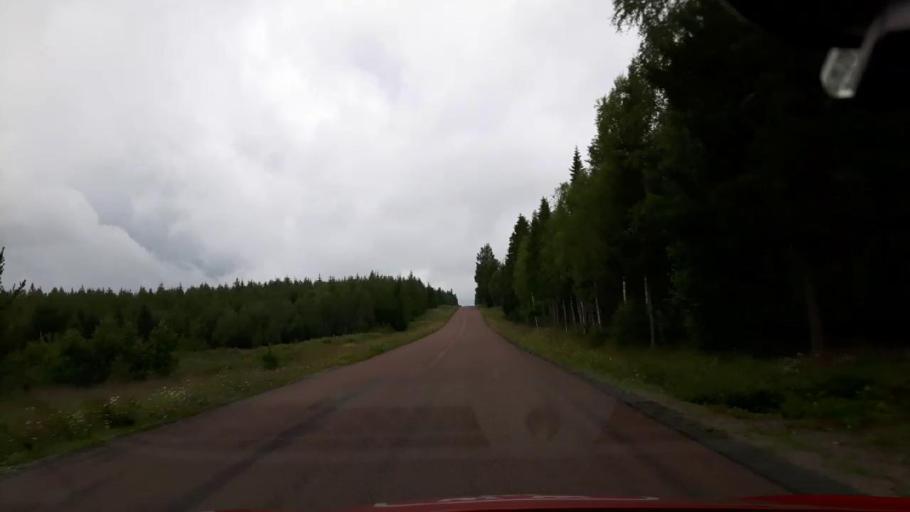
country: SE
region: Jaemtland
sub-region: Krokoms Kommun
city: Valla
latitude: 63.3698
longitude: 13.7517
